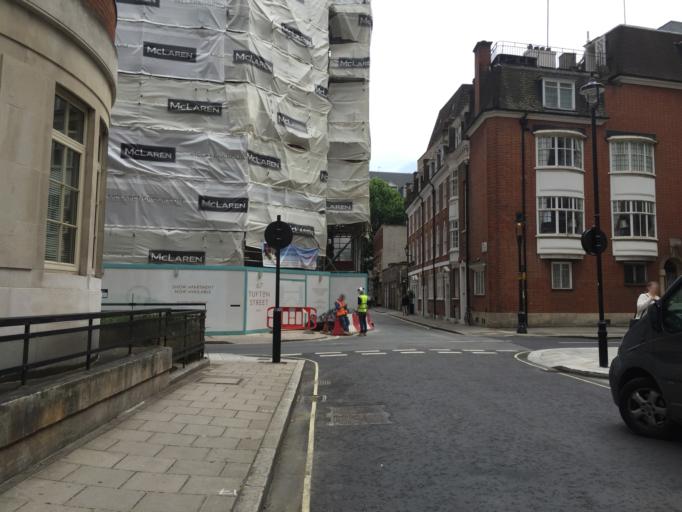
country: GB
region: England
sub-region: Greater London
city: City of Westminster
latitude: 51.4951
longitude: -0.1286
